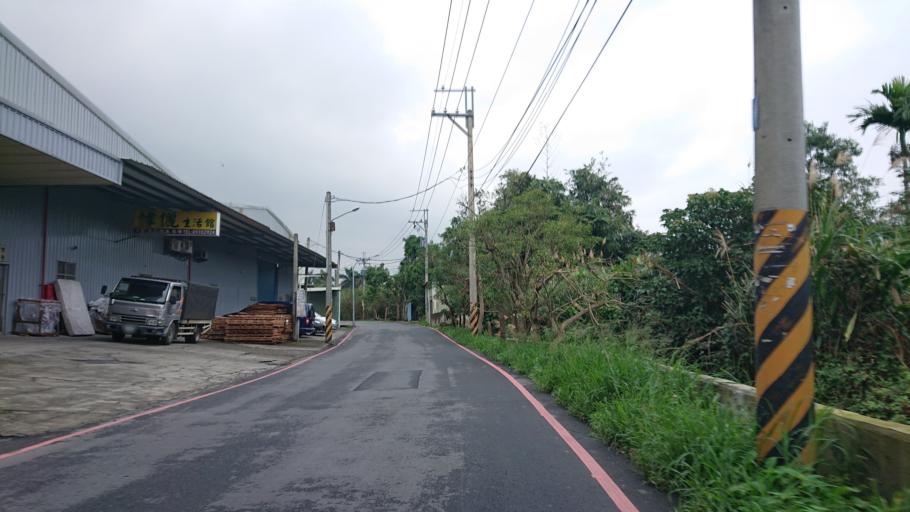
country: TW
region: Taiwan
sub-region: Taoyuan
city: Taoyuan
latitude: 24.9494
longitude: 121.3895
